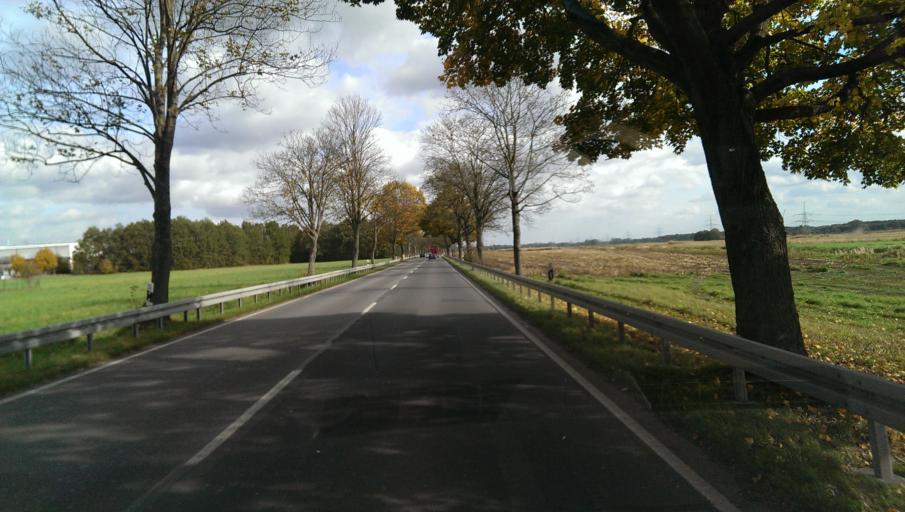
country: DE
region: Brandenburg
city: Lauchhammer
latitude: 51.4692
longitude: 13.8046
